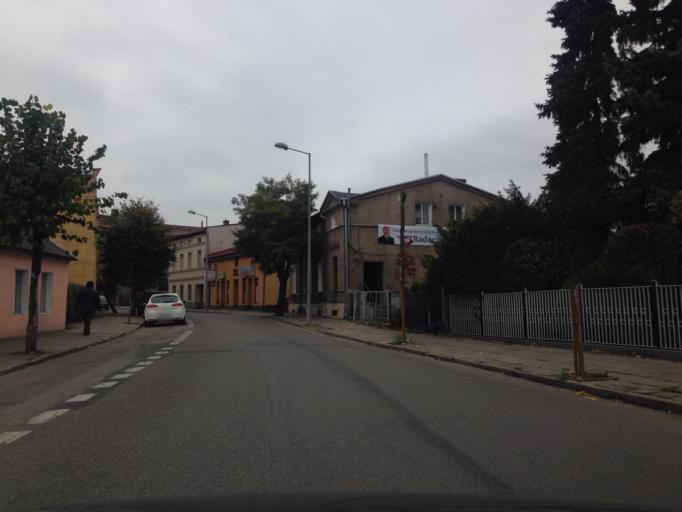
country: PL
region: Kujawsko-Pomorskie
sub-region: Powiat brodnicki
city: Brodnica
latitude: 53.2576
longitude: 19.4053
